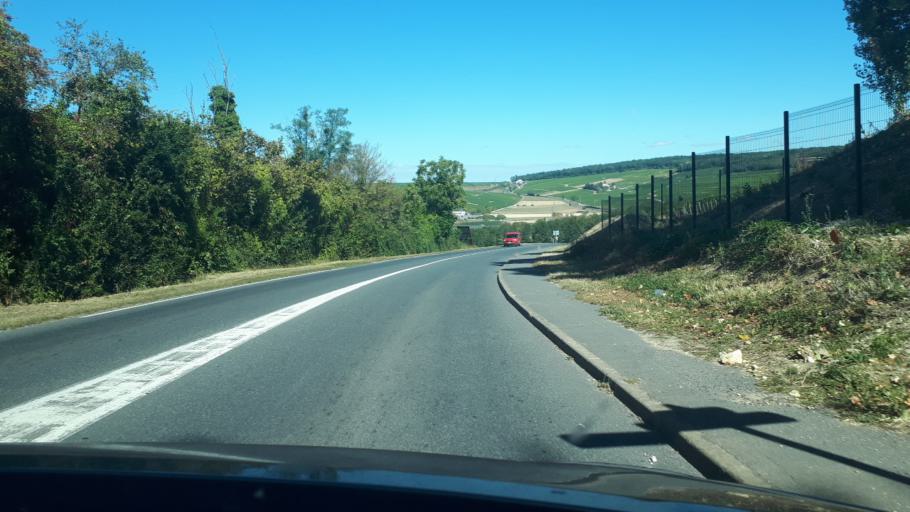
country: FR
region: Centre
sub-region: Departement du Cher
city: Sancerre
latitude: 47.3326
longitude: 2.8325
